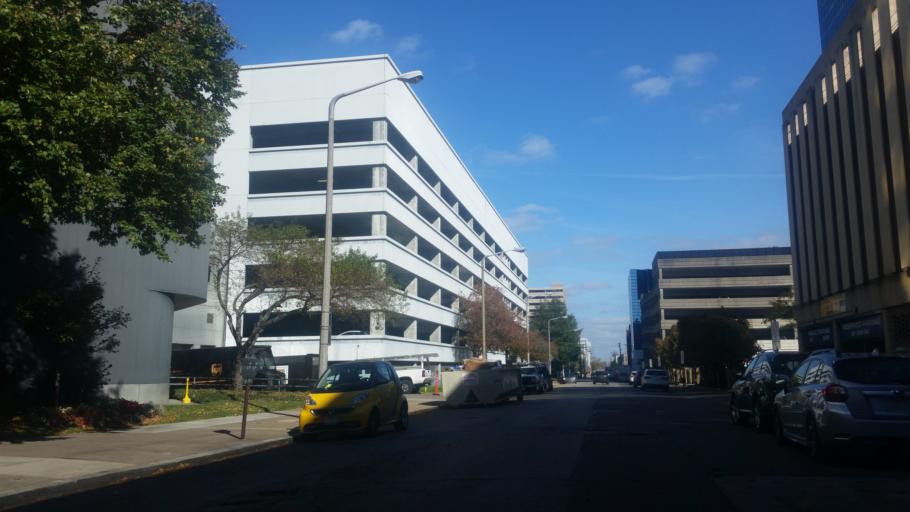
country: US
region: Ohio
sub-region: Cuyahoga County
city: Cleveland
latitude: 41.5034
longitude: -81.6891
